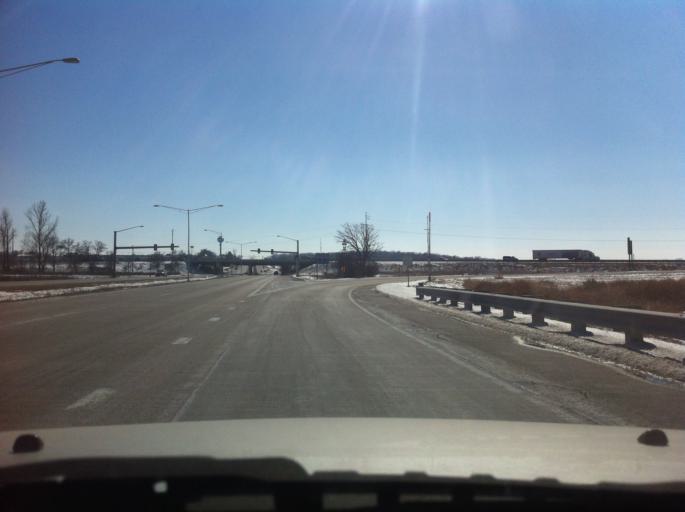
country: US
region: Wisconsin
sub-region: Dane County
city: Windsor
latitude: 43.1821
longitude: -89.3242
